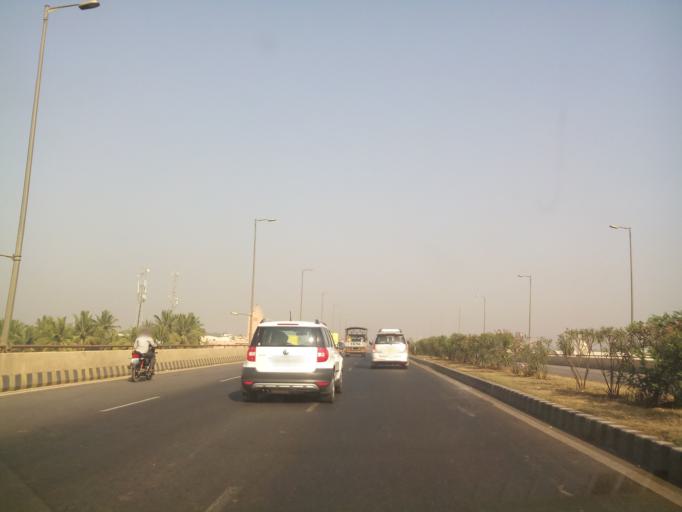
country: IN
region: Karnataka
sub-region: Bangalore Rural
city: Nelamangala
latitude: 13.0682
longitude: 77.4490
